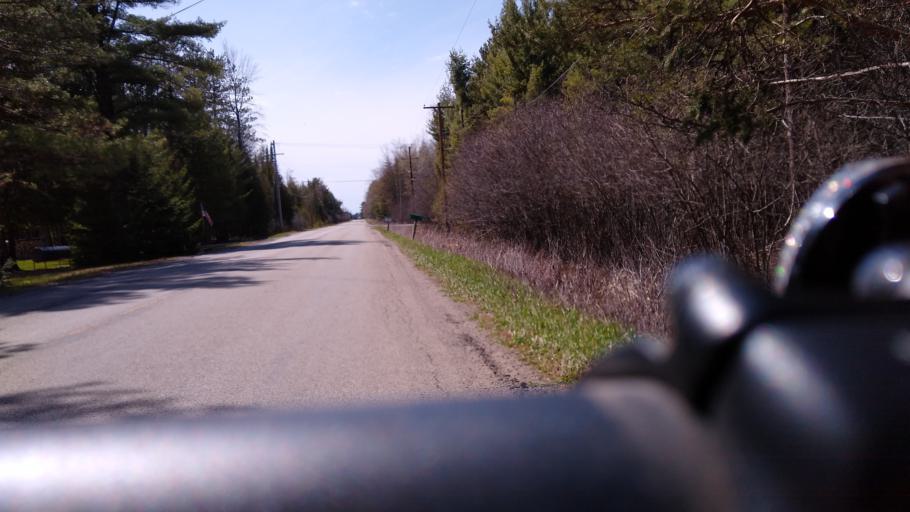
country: US
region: Michigan
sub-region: Delta County
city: Escanaba
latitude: 45.7353
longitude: -87.1713
